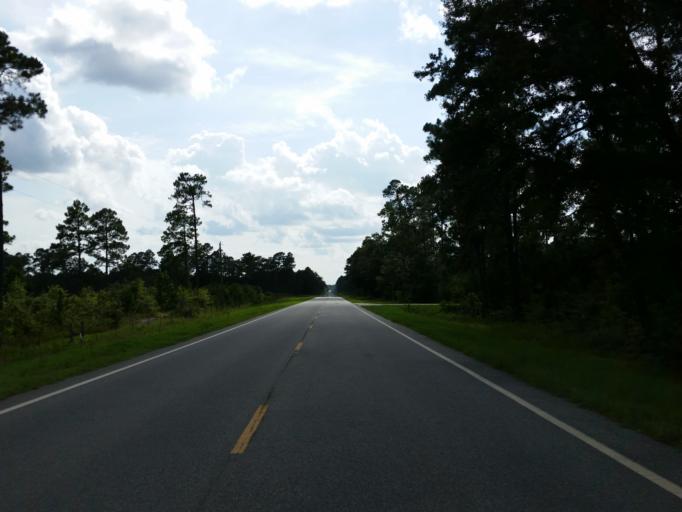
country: US
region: Georgia
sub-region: Lee County
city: Leesburg
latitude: 31.7281
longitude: -83.9698
